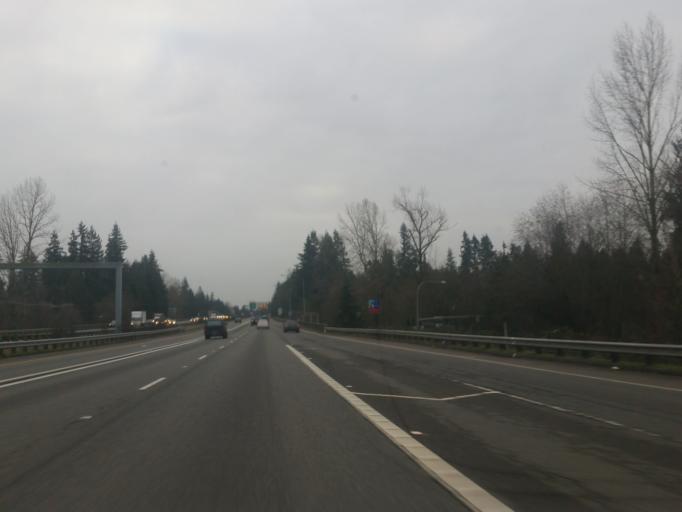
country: US
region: Washington
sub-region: King County
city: Bothell
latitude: 47.7921
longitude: -122.2092
